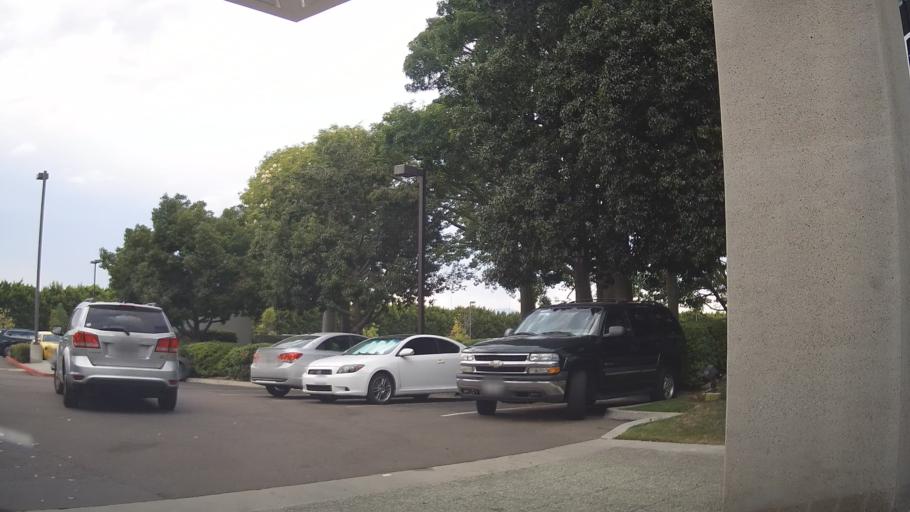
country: US
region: California
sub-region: San Diego County
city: San Diego
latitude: 32.8063
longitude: -117.1196
